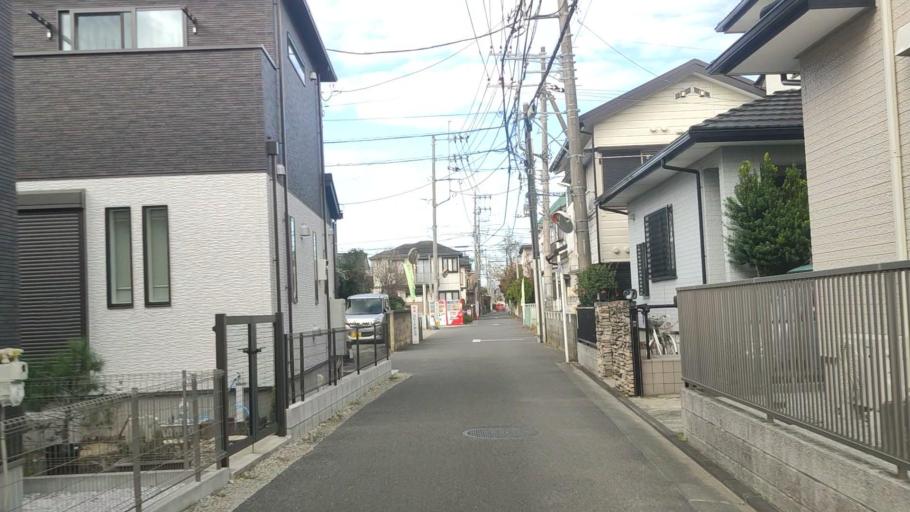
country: JP
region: Kanagawa
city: Minami-rinkan
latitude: 35.4895
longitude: 139.4379
